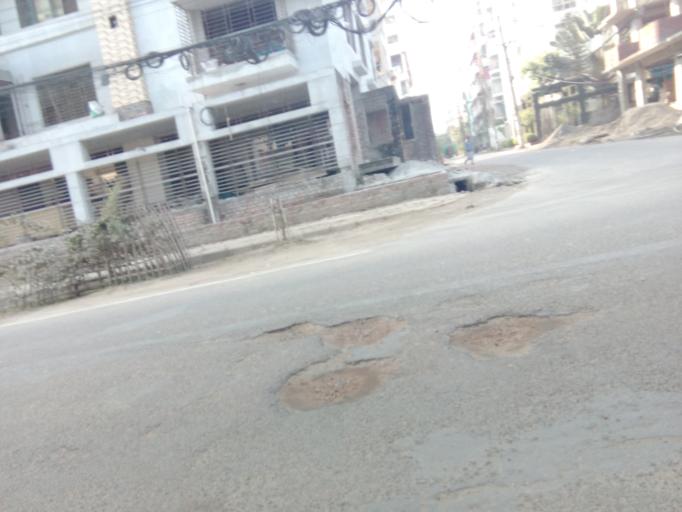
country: BD
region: Dhaka
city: Paltan
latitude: 23.8157
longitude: 90.4342
